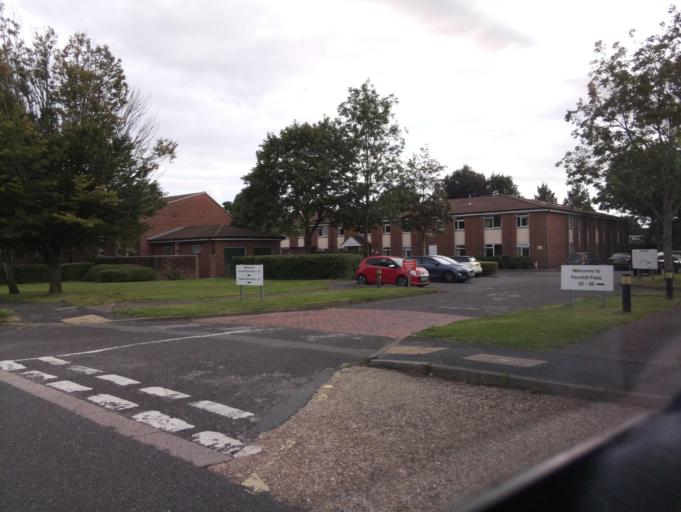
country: GB
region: England
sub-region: Hampshire
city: Eastleigh
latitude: 50.9844
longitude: -1.3691
